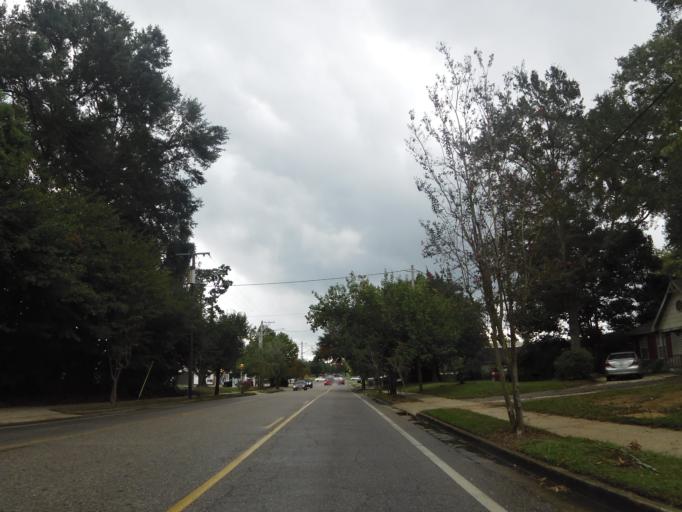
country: US
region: Alabama
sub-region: Baldwin County
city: Fairhope
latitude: 30.5236
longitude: -87.8882
